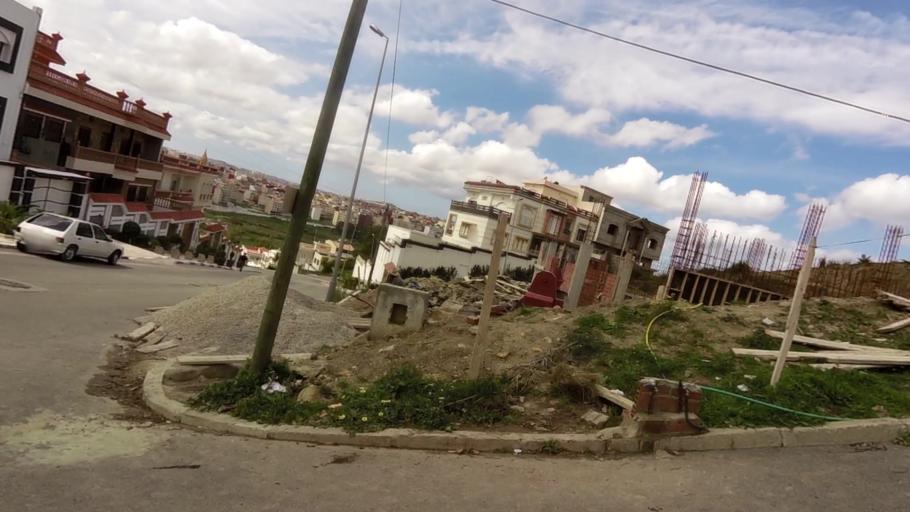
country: MA
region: Tanger-Tetouan
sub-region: Tanger-Assilah
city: Tangier
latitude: 35.7715
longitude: -5.7565
